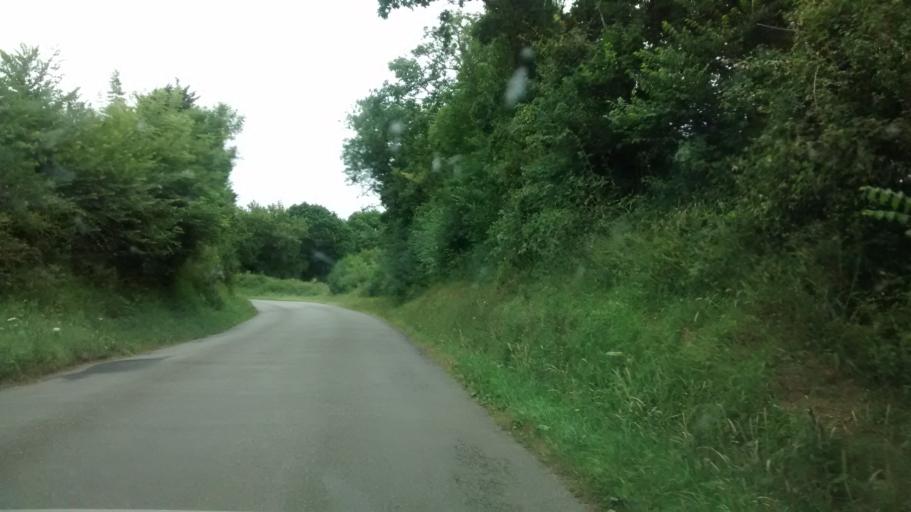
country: FR
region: Brittany
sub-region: Departement du Finistere
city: Plougastel-Daoulas
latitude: 48.3454
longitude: -4.3923
